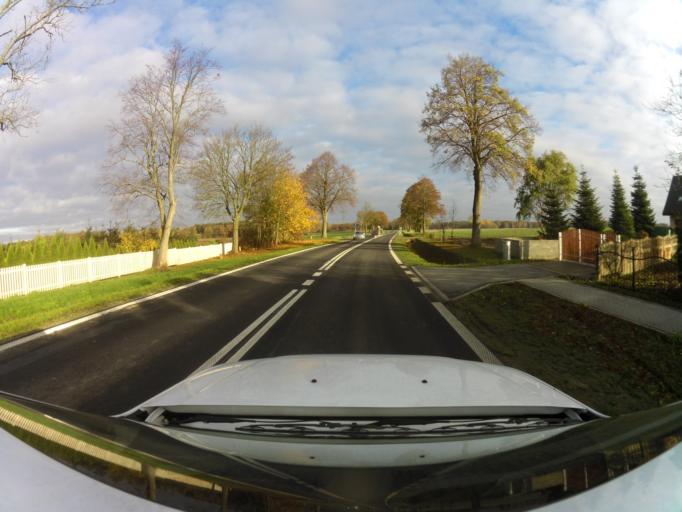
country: PL
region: West Pomeranian Voivodeship
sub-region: Powiat gryficki
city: Gryfice
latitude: 53.9803
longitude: 15.2376
